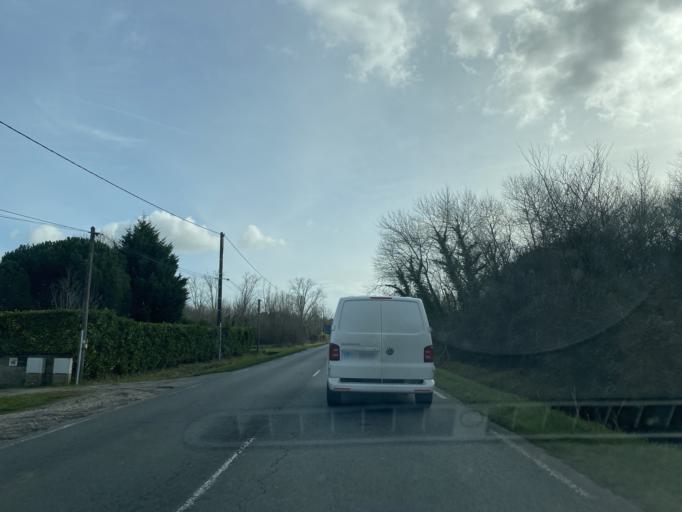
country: FR
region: Aquitaine
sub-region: Departement de la Gironde
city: Le Taillan-Medoc
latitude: 44.9250
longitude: -0.6764
